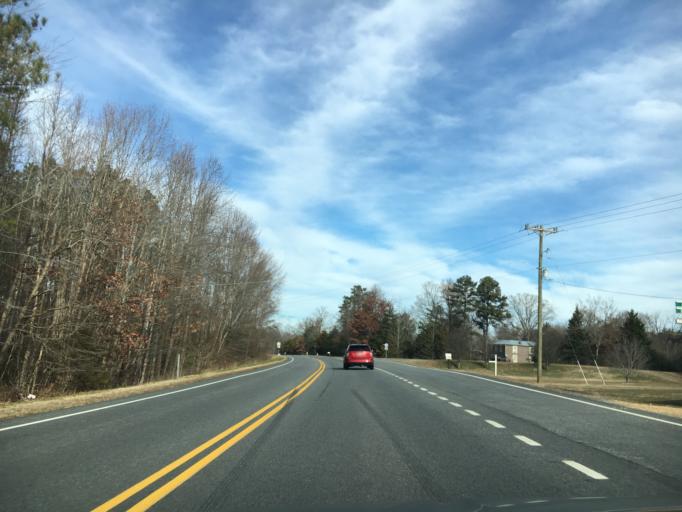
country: US
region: Virginia
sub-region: Louisa County
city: Louisa
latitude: 38.0374
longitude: -77.8875
